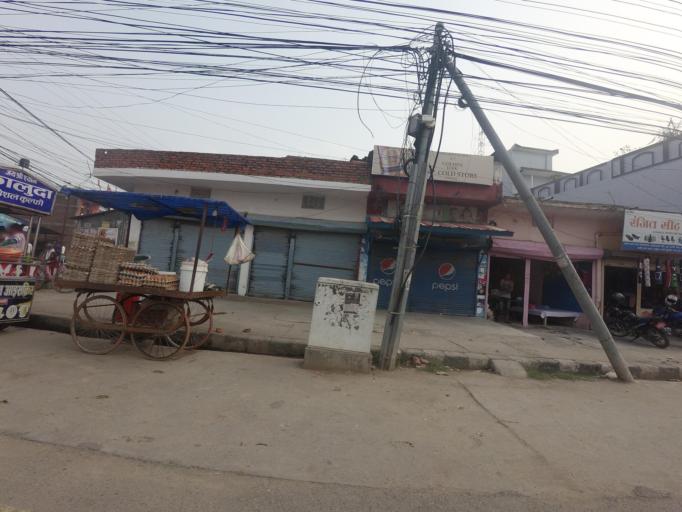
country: NP
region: Western Region
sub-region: Lumbini Zone
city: Bhairahawa
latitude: 27.5074
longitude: 83.4414
